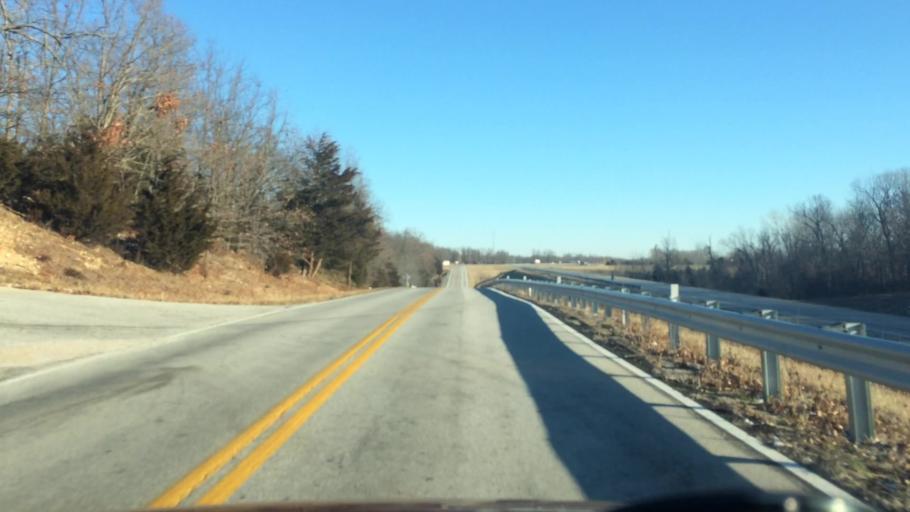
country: US
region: Missouri
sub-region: Greene County
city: Strafford
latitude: 37.2783
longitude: -93.0466
